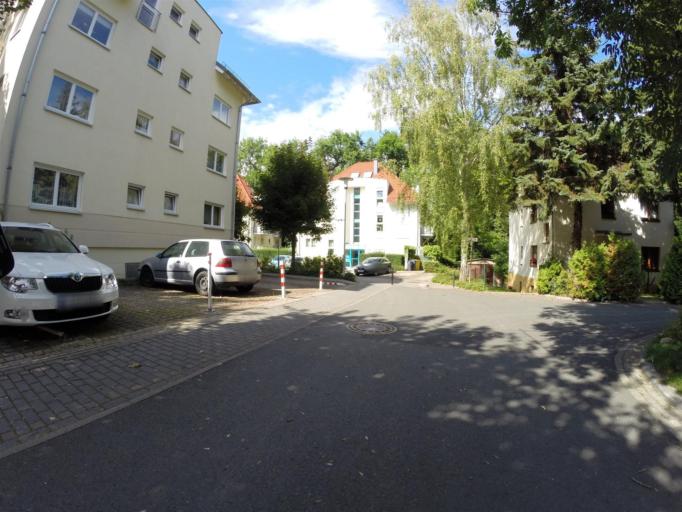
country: DE
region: Thuringia
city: Jena
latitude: 50.9323
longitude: 11.5702
